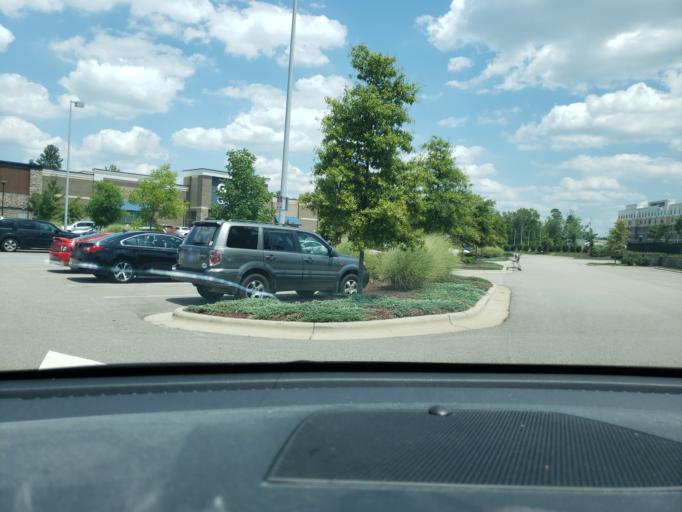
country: US
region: North Carolina
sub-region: Wake County
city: Green Level
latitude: 35.8471
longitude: -78.8881
